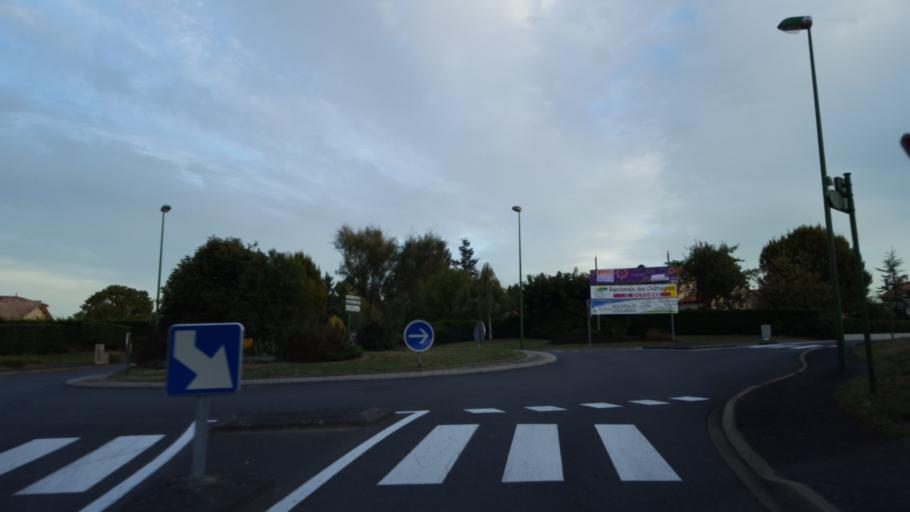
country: FR
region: Pays de la Loire
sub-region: Departement de la Loire-Atlantique
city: Haute-Goulaine
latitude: 47.1992
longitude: -1.4385
